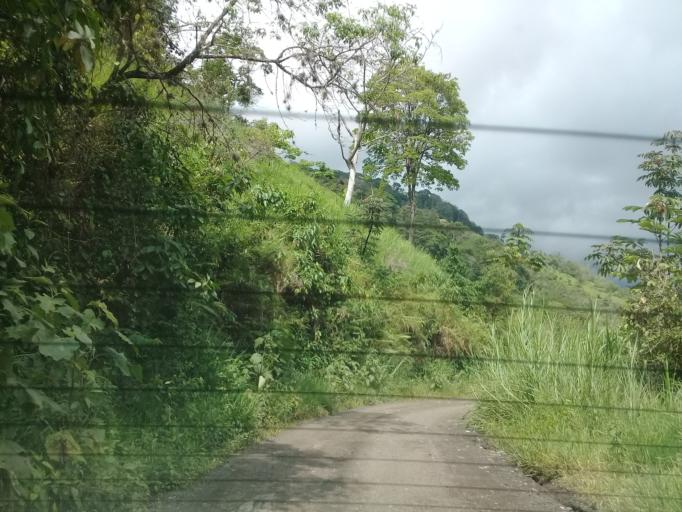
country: CO
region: Cundinamarca
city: Quipile
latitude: 4.7201
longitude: -74.5401
